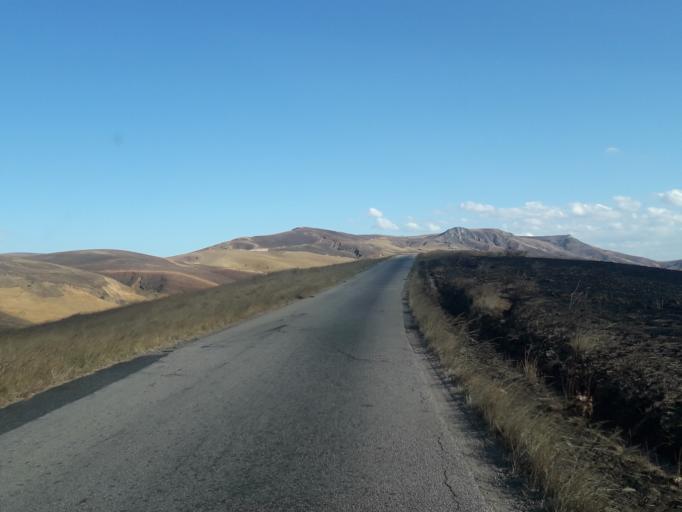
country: MG
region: Analamanga
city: Ankazobe
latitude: -17.7920
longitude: 47.0207
